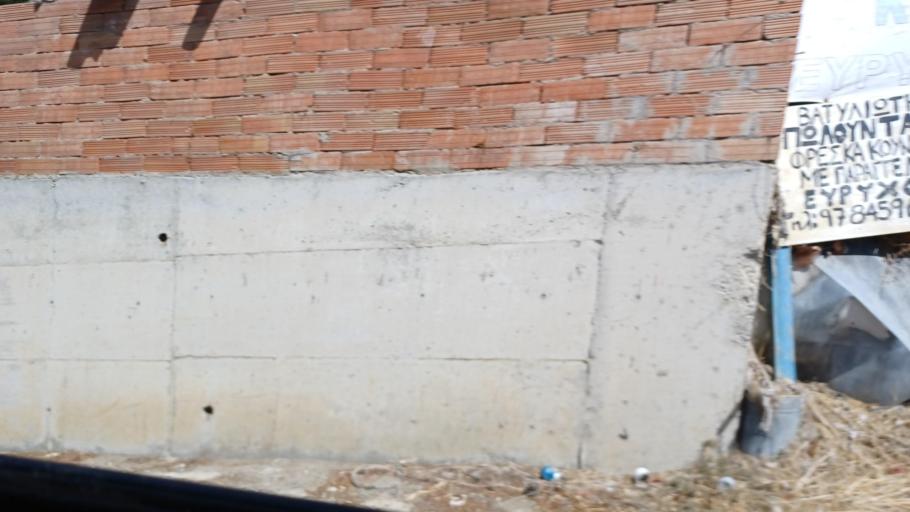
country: CY
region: Lefkosia
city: Kakopetria
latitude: 35.0492
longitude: 32.8963
